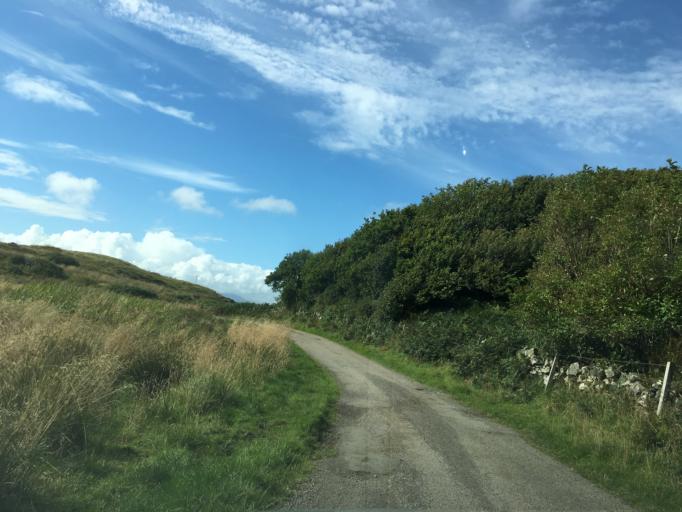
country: GB
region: Scotland
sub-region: Argyll and Bute
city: Oban
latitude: 56.2466
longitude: -5.6334
